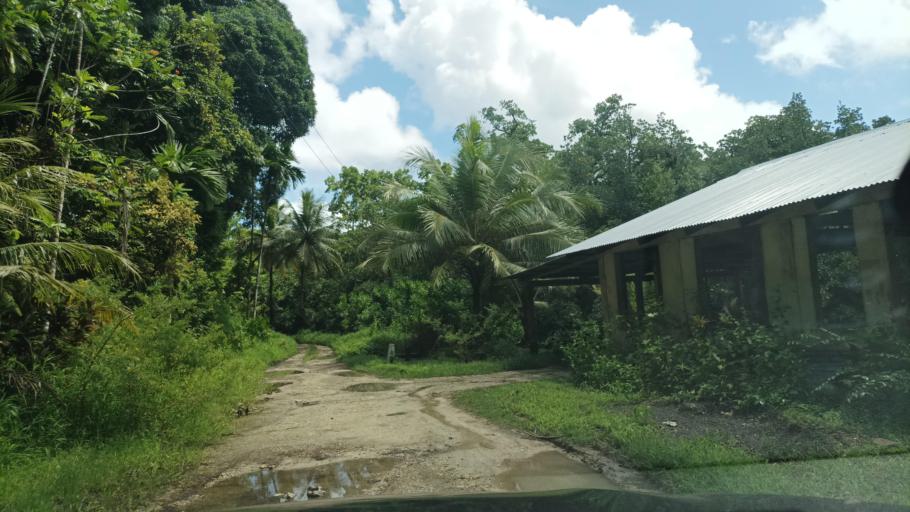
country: FM
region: Pohnpei
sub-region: Sokehs Municipality
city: Palikir - National Government Center
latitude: 6.9446
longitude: 158.1615
